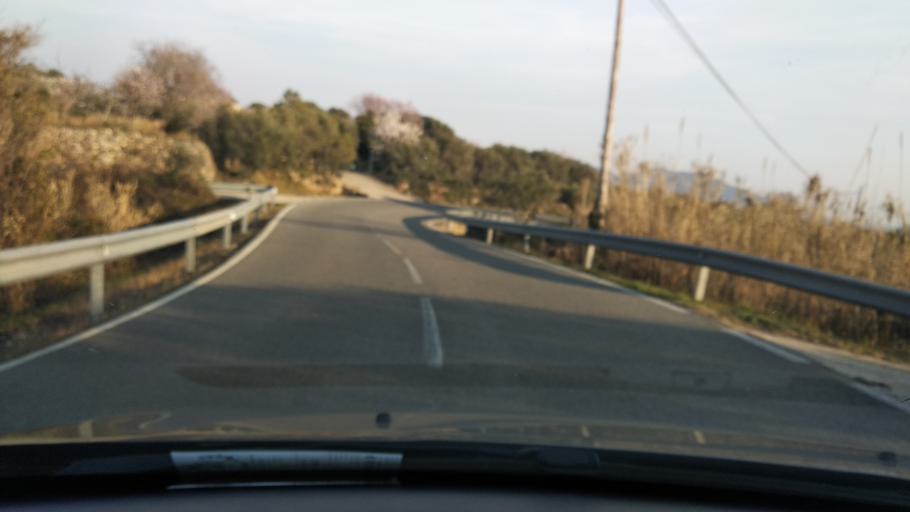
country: ES
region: Catalonia
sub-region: Provincia de Tarragona
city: Alforja
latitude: 41.2168
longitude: 0.9719
